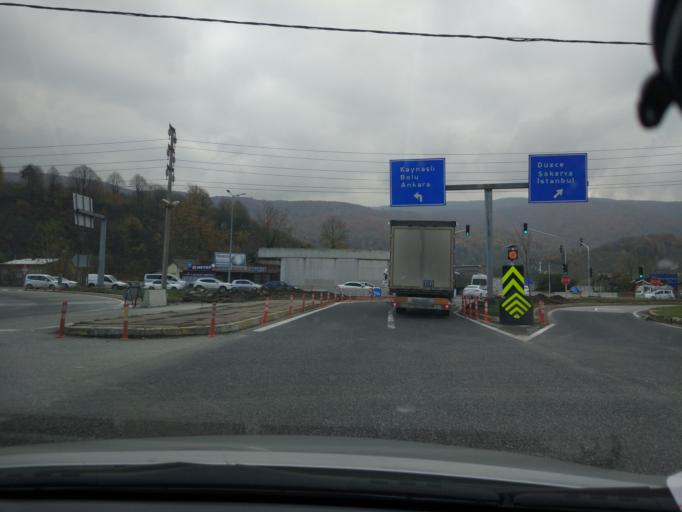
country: TR
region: Duzce
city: Kaynasli
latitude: 40.7826
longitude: 31.2775
